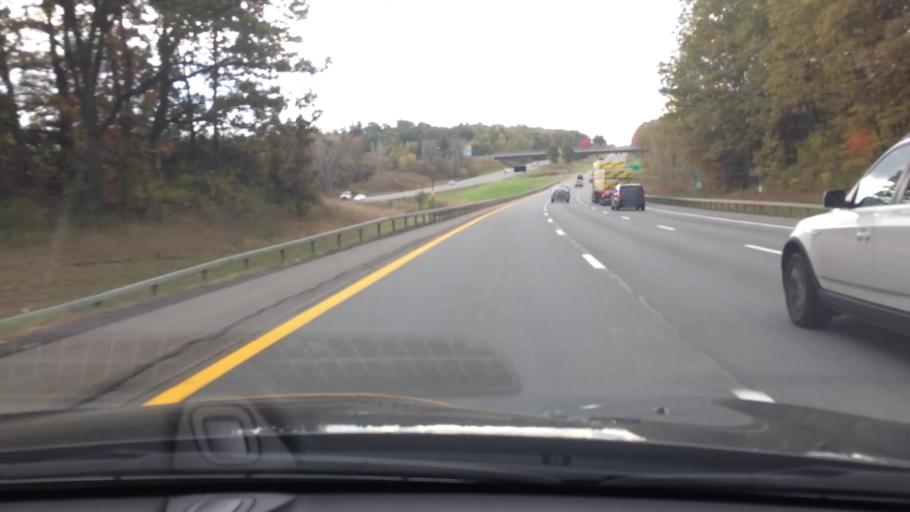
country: US
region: New York
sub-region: Saratoga County
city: Country Knolls
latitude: 42.8942
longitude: -73.7808
